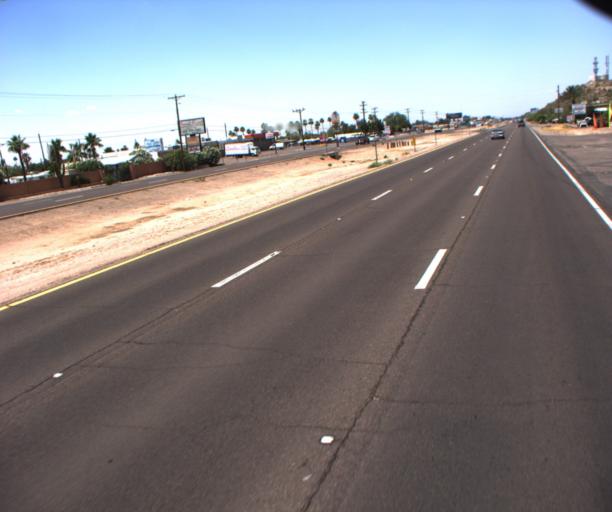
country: US
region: Arizona
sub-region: Pinal County
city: Apache Junction
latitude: 33.4154
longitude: -111.6448
